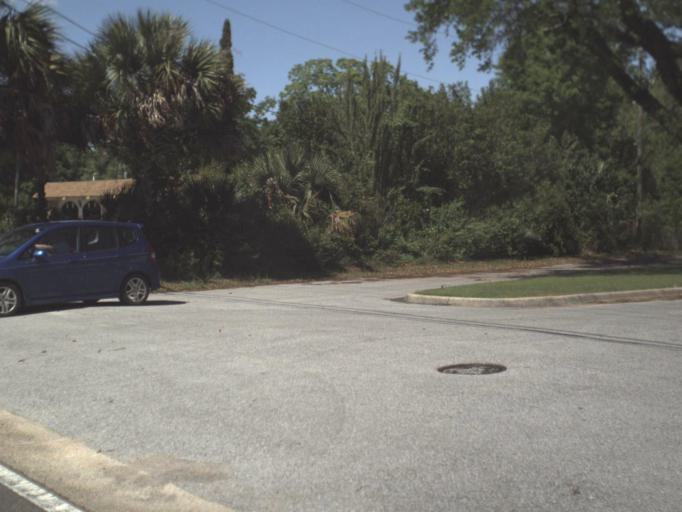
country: US
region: Florida
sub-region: Escambia County
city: Brent
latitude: 30.4709
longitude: -87.2249
